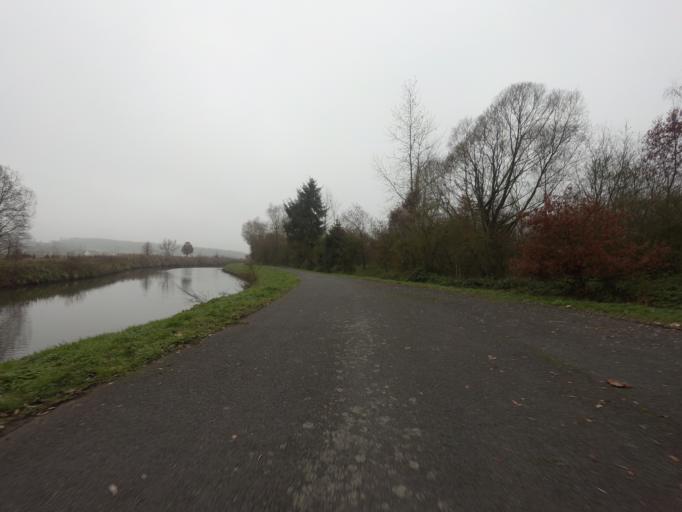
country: BE
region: Flanders
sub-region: Provincie Oost-Vlaanderen
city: Geraardsbergen
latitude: 50.7578
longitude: 3.8626
